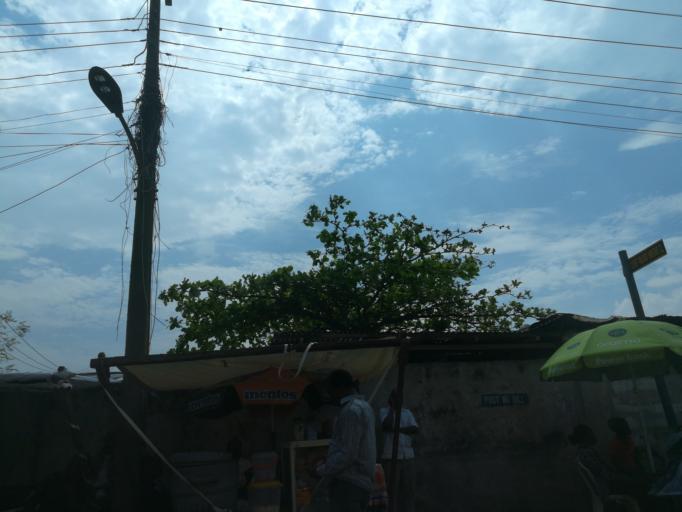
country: NG
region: Lagos
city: Oshodi
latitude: 6.5451
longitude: 3.3296
